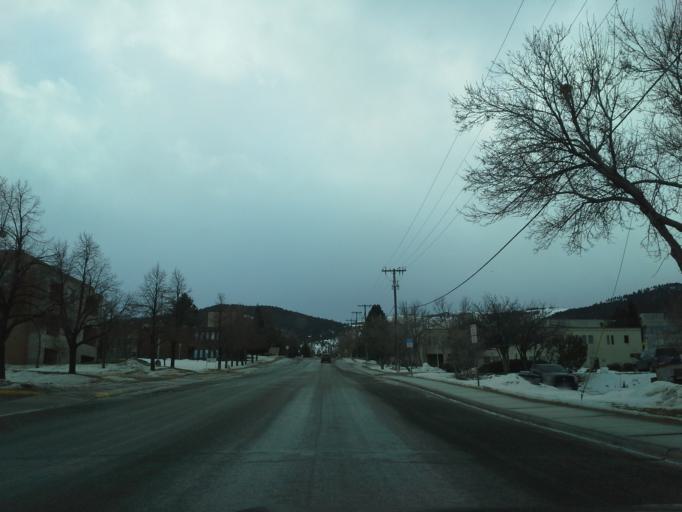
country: US
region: Montana
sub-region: Lewis and Clark County
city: Helena
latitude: 46.5884
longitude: -112.0148
